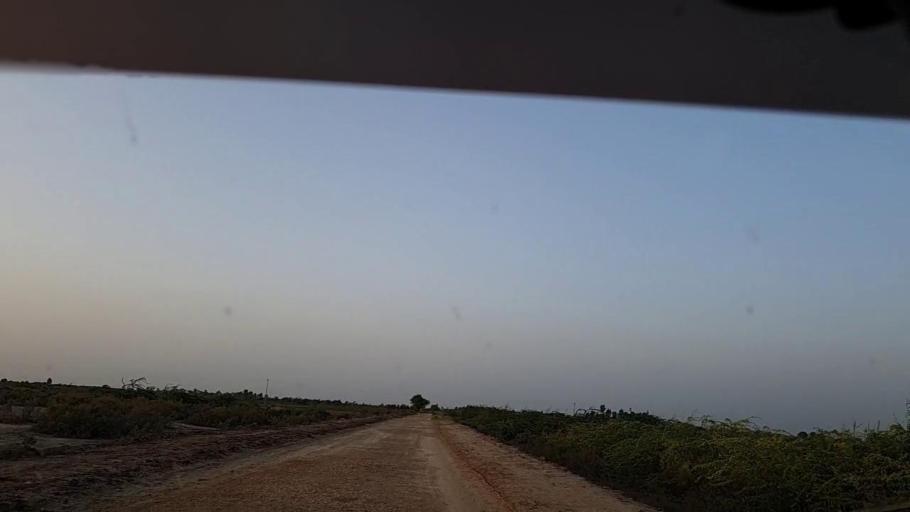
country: PK
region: Sindh
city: Kadhan
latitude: 24.5269
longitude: 68.9436
